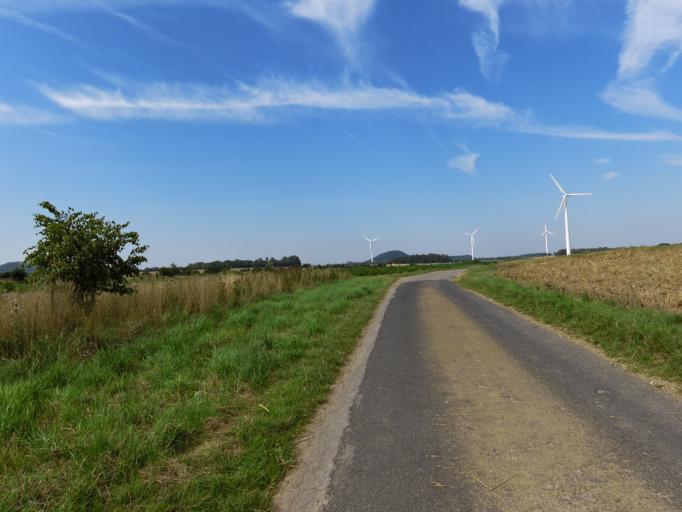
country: DE
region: North Rhine-Westphalia
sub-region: Regierungsbezirk Koln
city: Alsdorf
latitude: 50.8923
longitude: 6.1668
